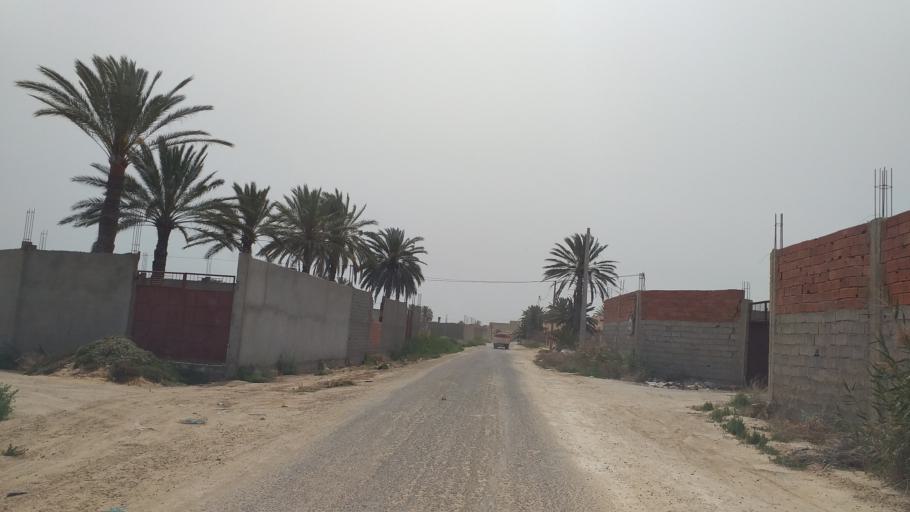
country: TN
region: Qabis
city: Gabes
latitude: 33.9447
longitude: 10.0538
